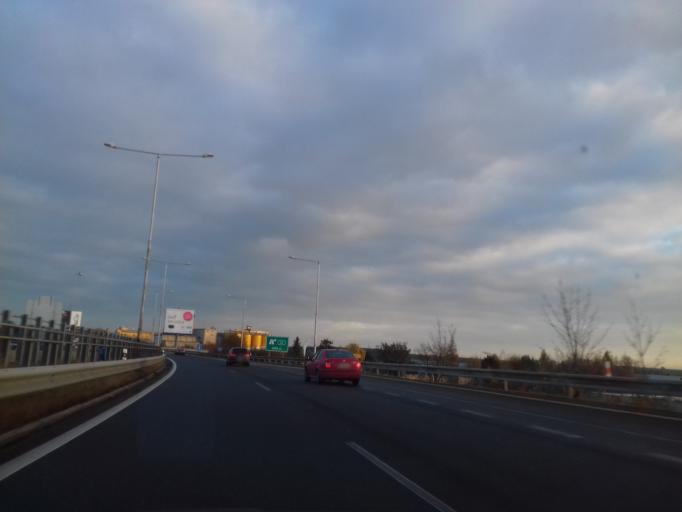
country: CZ
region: Olomoucky
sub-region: Okres Prostejov
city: Prostejov
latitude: 49.4705
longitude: 17.1337
